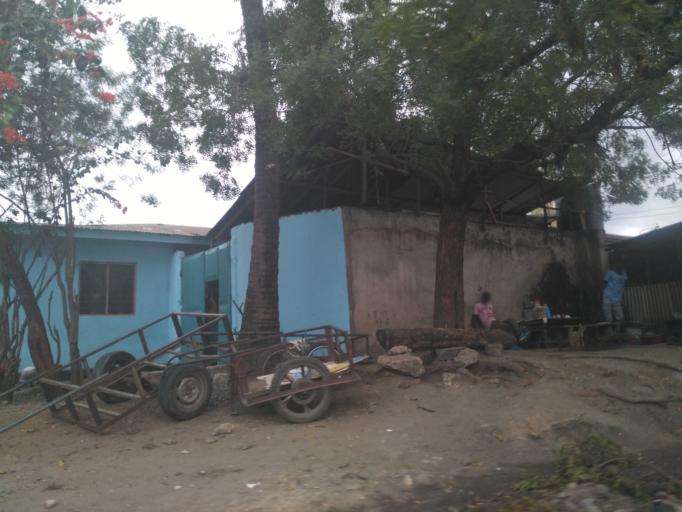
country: TZ
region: Dar es Salaam
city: Magomeni
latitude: -6.7919
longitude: 39.2677
